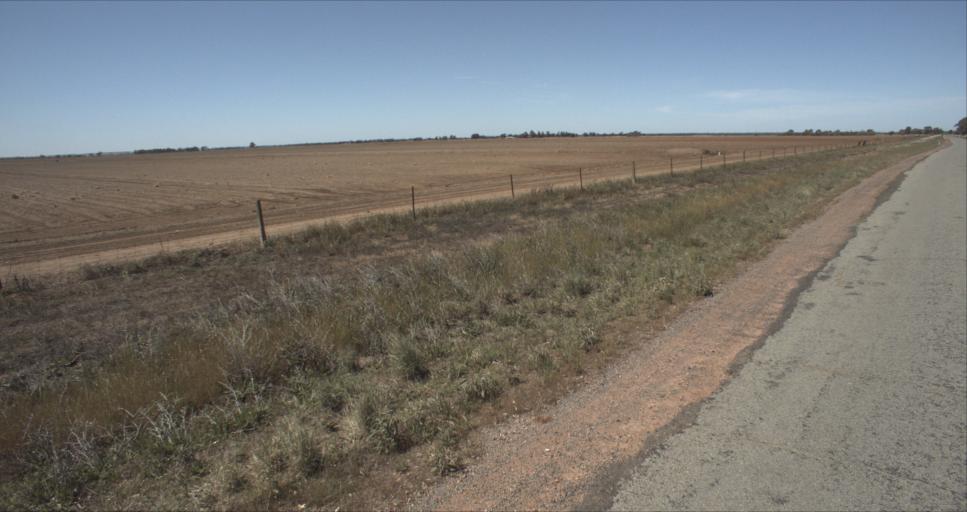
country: AU
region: New South Wales
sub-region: Leeton
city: Leeton
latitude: -34.5568
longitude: 146.3135
